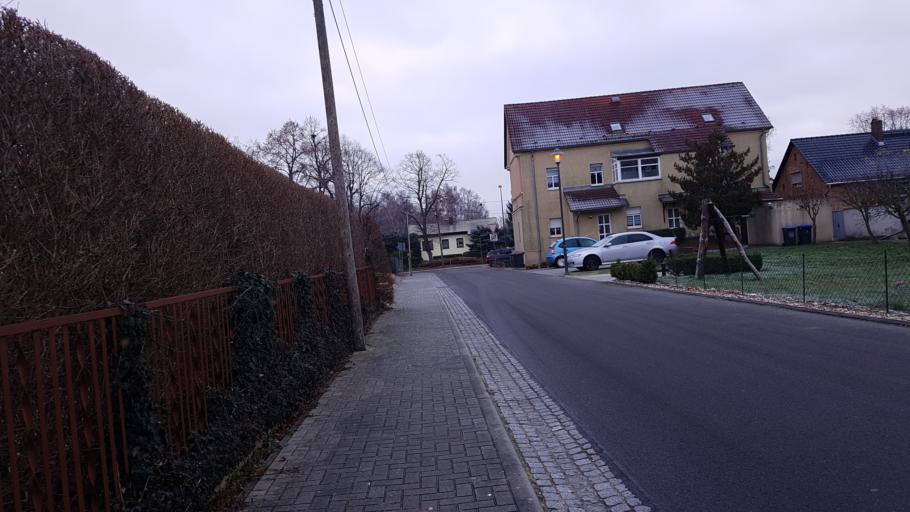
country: DE
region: Brandenburg
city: Schipkau
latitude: 51.5411
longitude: 13.8888
